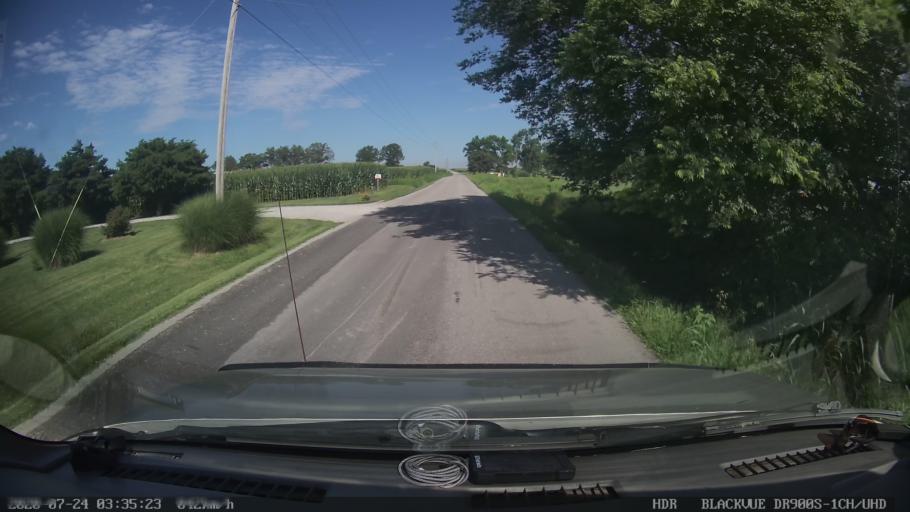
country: US
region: Kentucky
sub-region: Todd County
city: Guthrie
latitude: 36.7101
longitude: -87.2252
